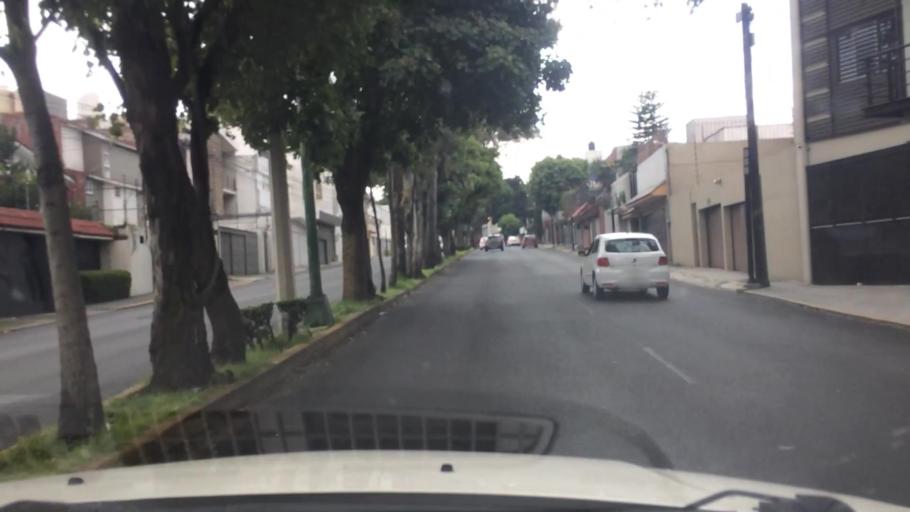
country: MX
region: Mexico City
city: Magdalena Contreras
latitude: 19.3473
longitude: -99.2341
